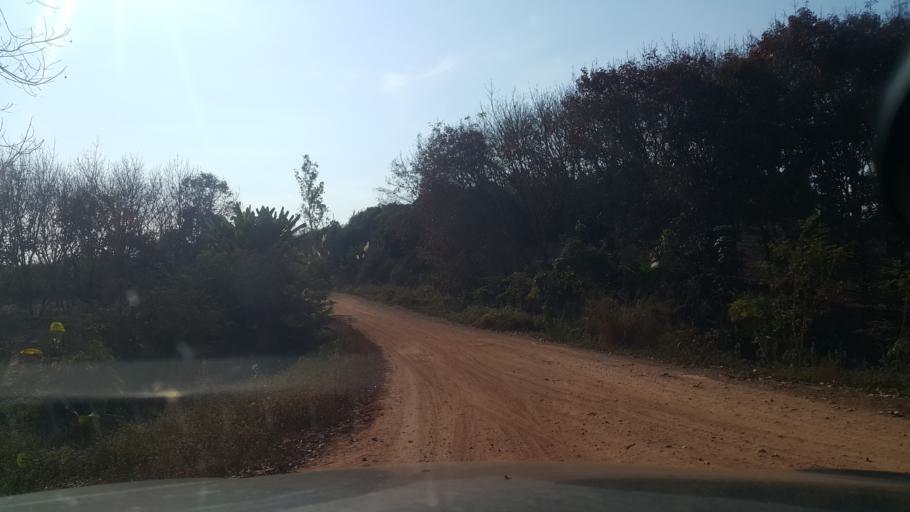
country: TH
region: Loei
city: Chiang Khan
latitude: 17.8106
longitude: 101.6177
